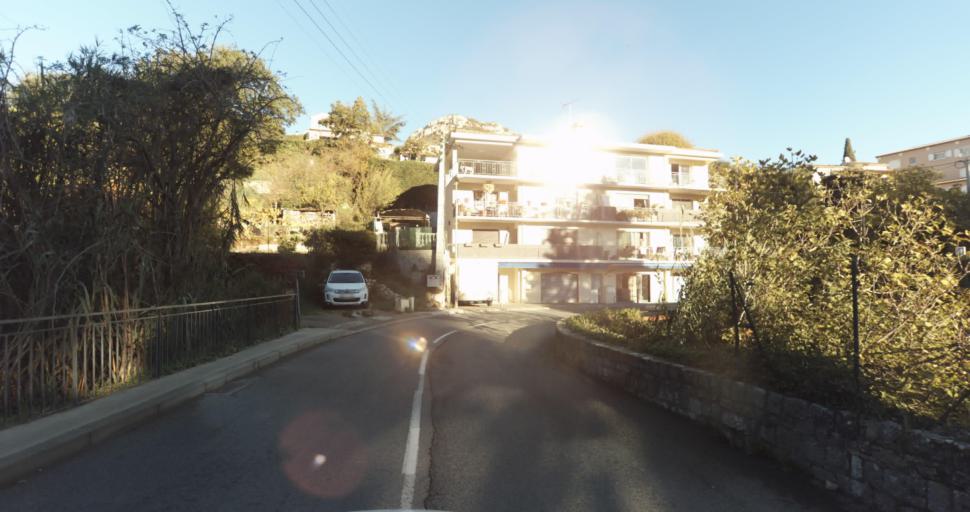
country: FR
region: Provence-Alpes-Cote d'Azur
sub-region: Departement des Alpes-Maritimes
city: Vence
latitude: 43.7244
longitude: 7.1128
